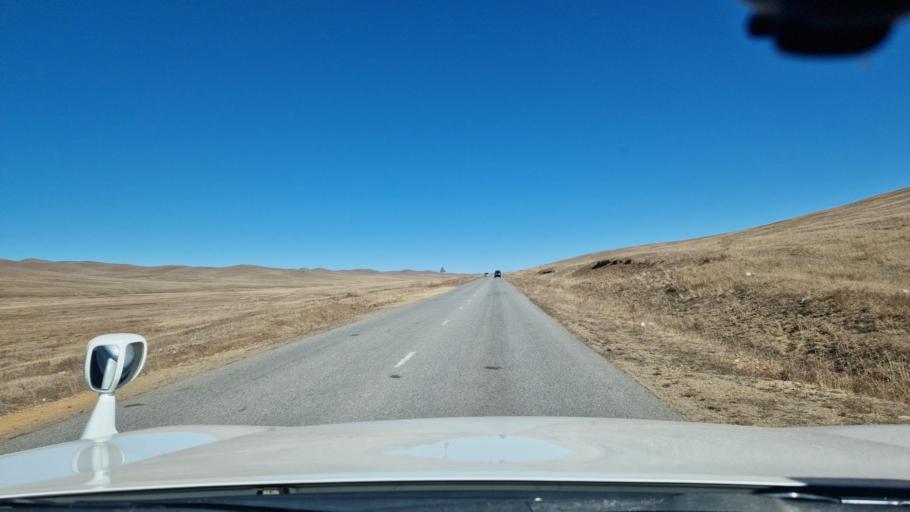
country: MN
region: Hentiy
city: Modot
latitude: 47.7290
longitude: 108.5906
